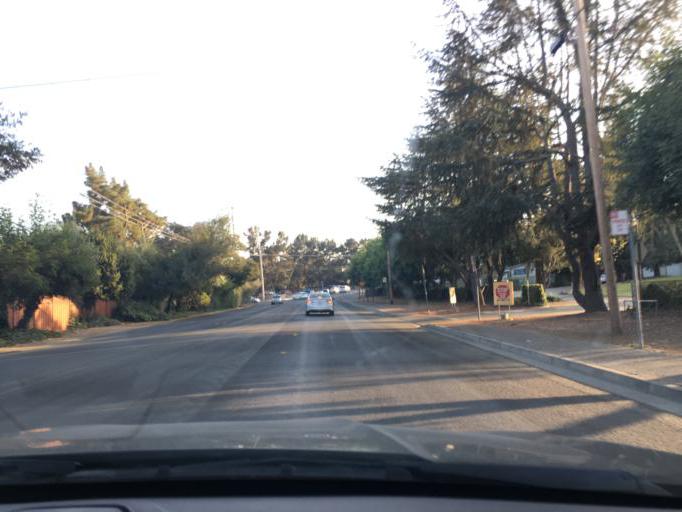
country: US
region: California
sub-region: Santa Clara County
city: Loyola
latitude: 37.3472
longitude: -122.0779
